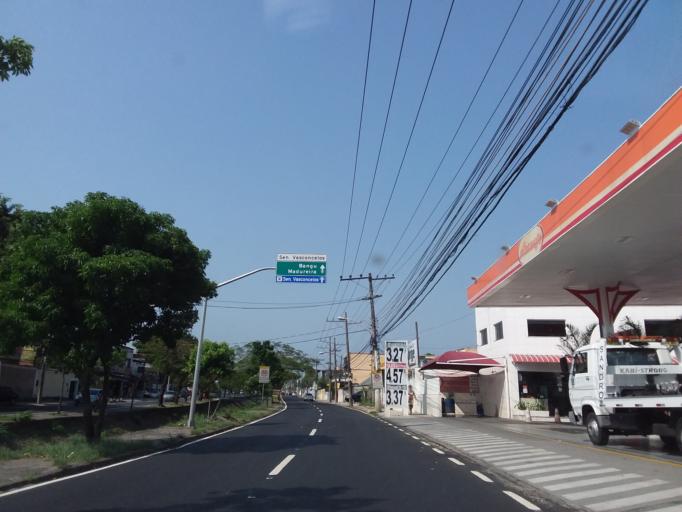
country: BR
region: Rio de Janeiro
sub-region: Nilopolis
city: Nilopolis
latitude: -22.9011
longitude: -43.5438
